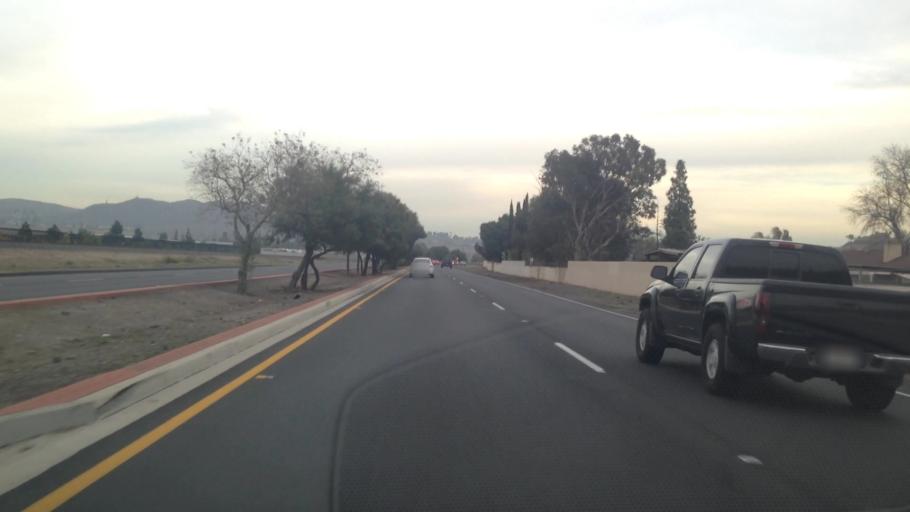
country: US
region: California
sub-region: Riverside County
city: Glen Avon
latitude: 34.0008
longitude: -117.4917
